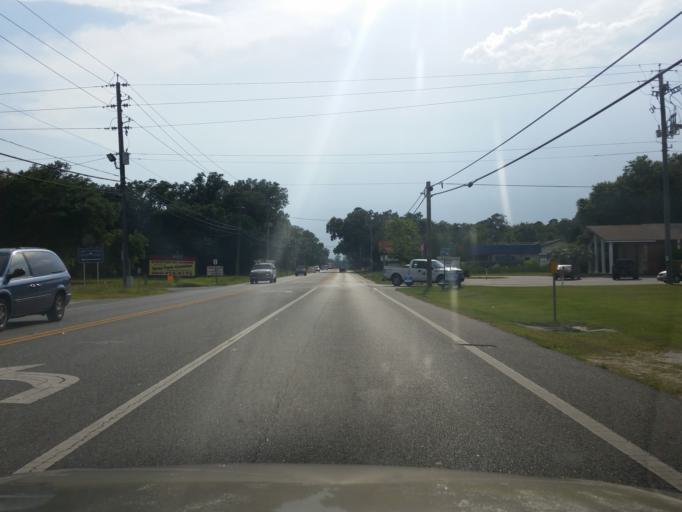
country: US
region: Florida
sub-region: Escambia County
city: Ferry Pass
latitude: 30.5101
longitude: -87.2102
